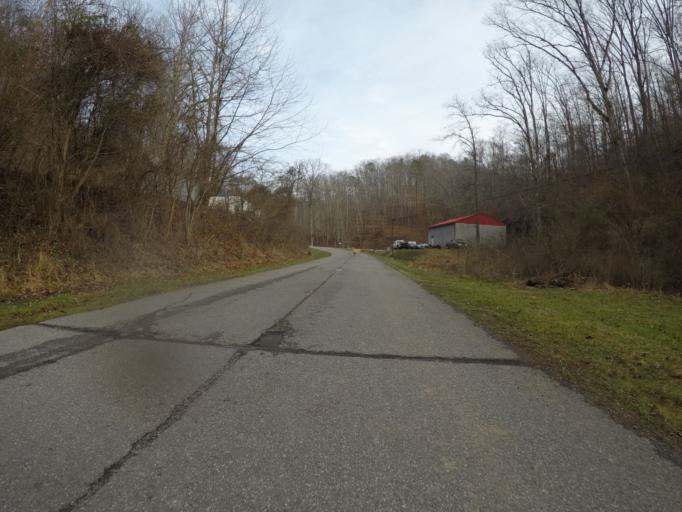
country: US
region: West Virginia
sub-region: Wayne County
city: Lavalette
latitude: 38.3382
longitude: -82.3766
